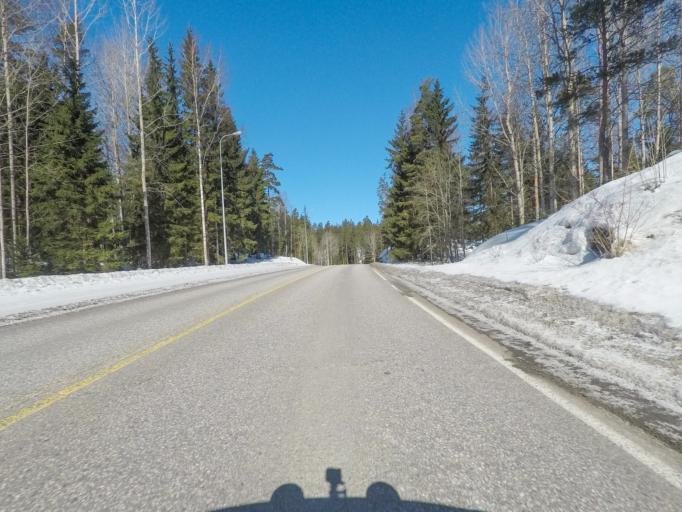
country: FI
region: Uusimaa
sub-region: Helsinki
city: Espoo
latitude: 60.2856
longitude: 24.5826
